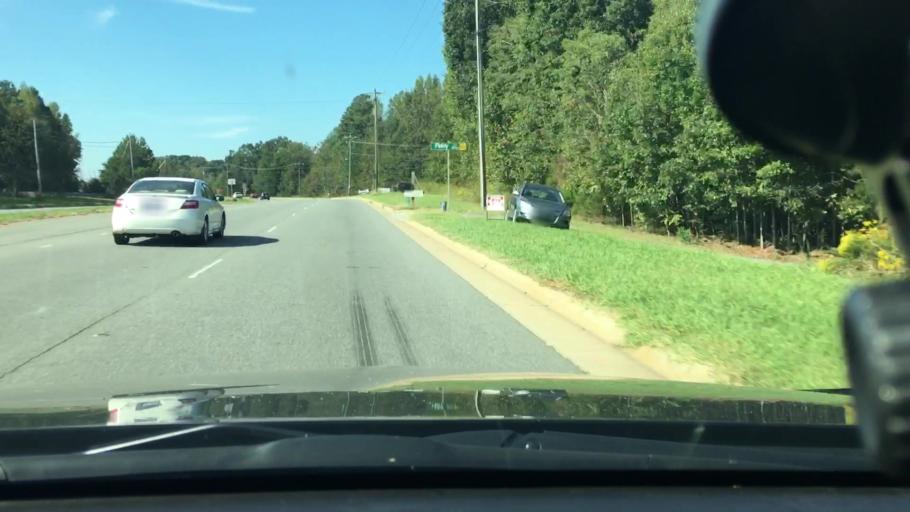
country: US
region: North Carolina
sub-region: Mecklenburg County
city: Mint Hill
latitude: 35.2329
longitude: -80.6037
